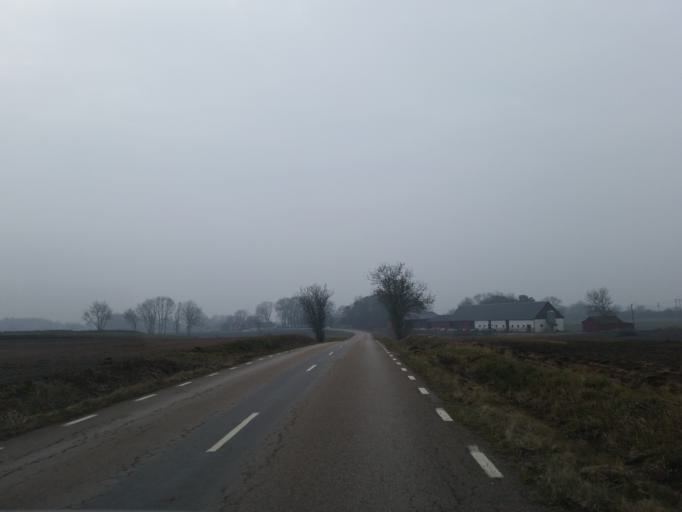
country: SE
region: Kalmar
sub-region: Morbylanga Kommun
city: Moerbylanga
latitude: 56.4247
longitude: 16.4158
